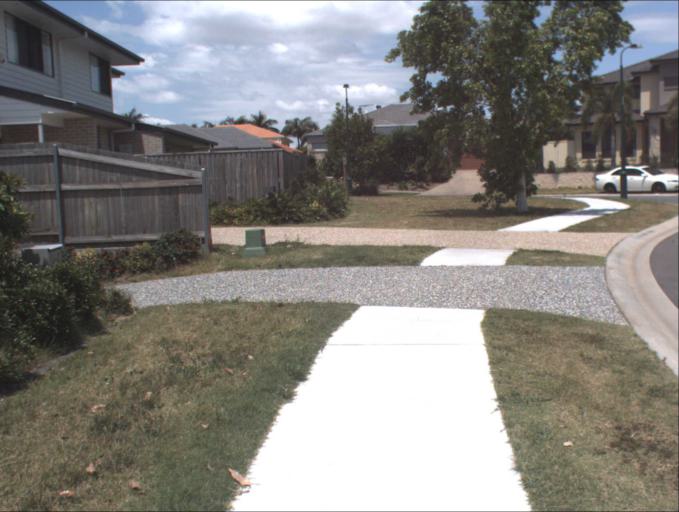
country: AU
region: Queensland
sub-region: Logan
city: Rochedale South
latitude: -27.5971
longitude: 153.1069
